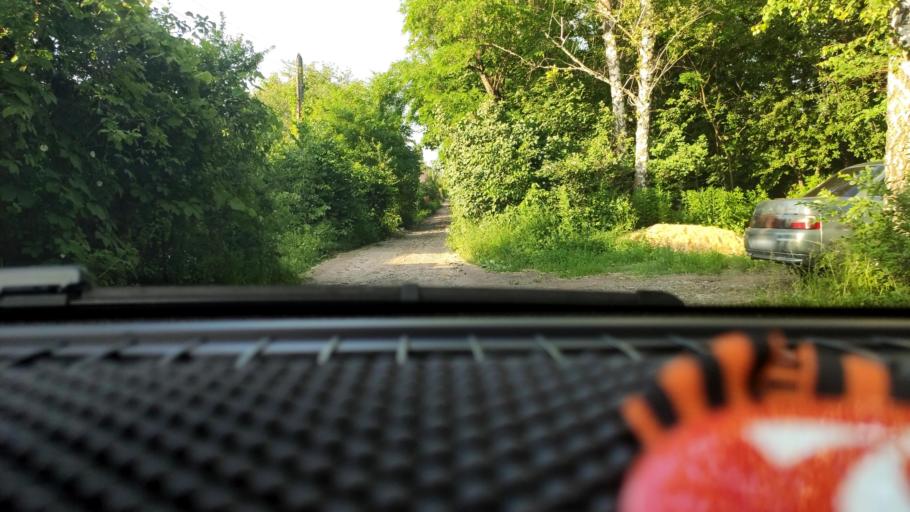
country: RU
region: Voronezj
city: Maslovka
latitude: 51.5935
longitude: 39.1708
